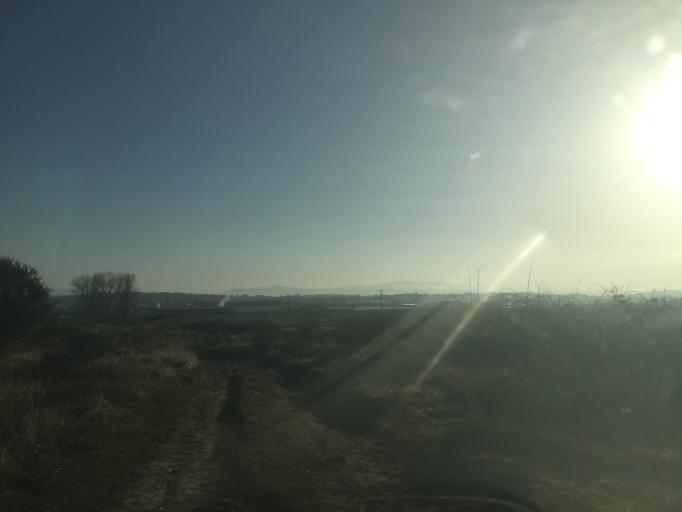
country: ES
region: Castille and Leon
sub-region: Provincia de Burgos
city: Medina de Pomar
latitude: 42.9237
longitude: -3.5899
